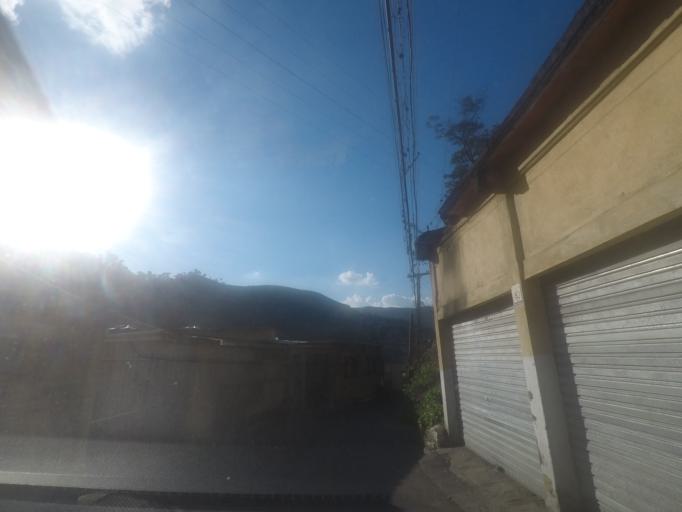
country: BR
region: Rio de Janeiro
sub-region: Petropolis
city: Petropolis
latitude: -22.4985
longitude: -43.1467
